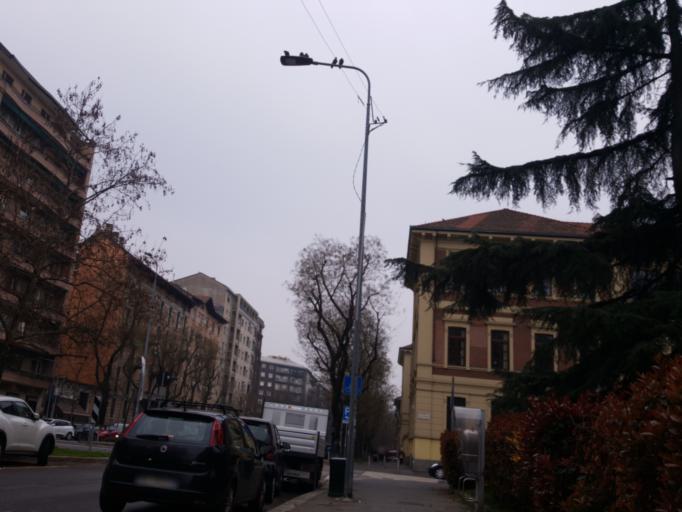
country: IT
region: Lombardy
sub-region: Citta metropolitana di Milano
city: Milano
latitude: 45.4571
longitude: 9.1615
